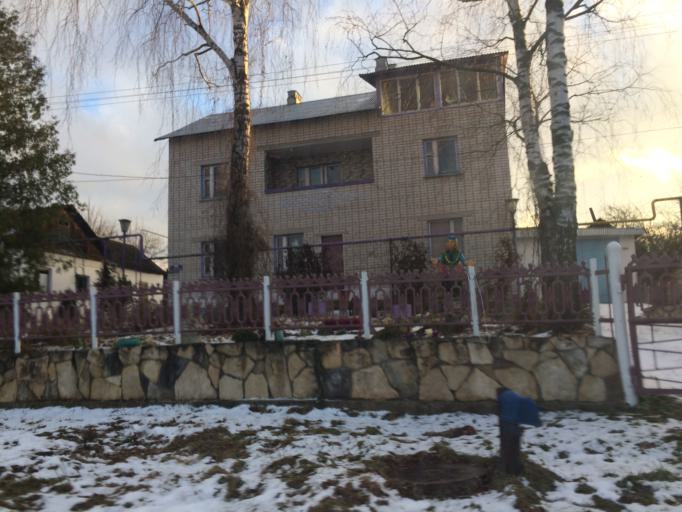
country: RU
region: Tula
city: Cherepet'
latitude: 54.1171
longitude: 36.3410
